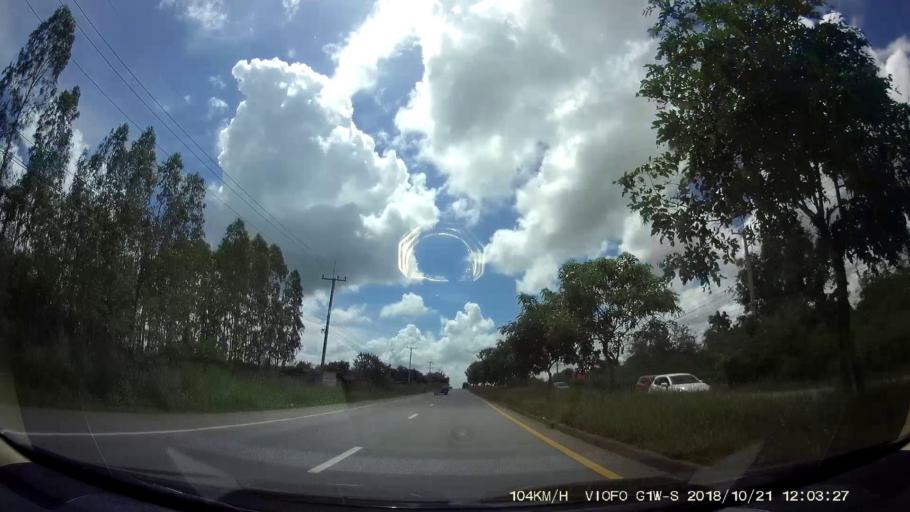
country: TH
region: Chaiyaphum
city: Chatturat
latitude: 15.5091
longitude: 101.8221
